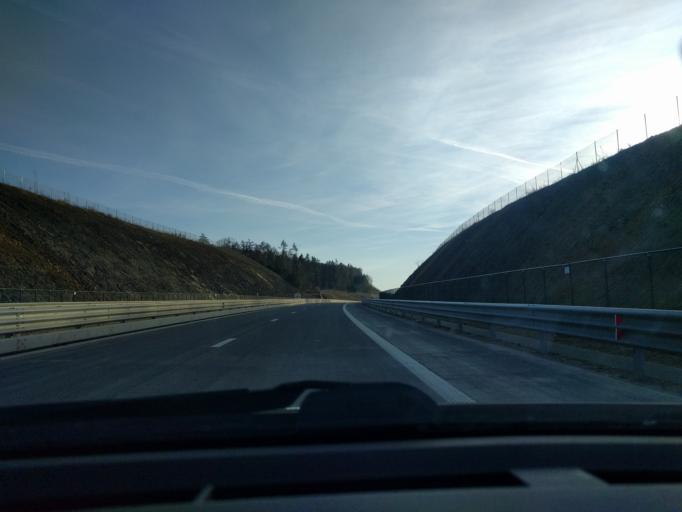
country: BE
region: Wallonia
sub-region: Province de Namur
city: Couvin
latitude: 50.0454
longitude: 4.5118
